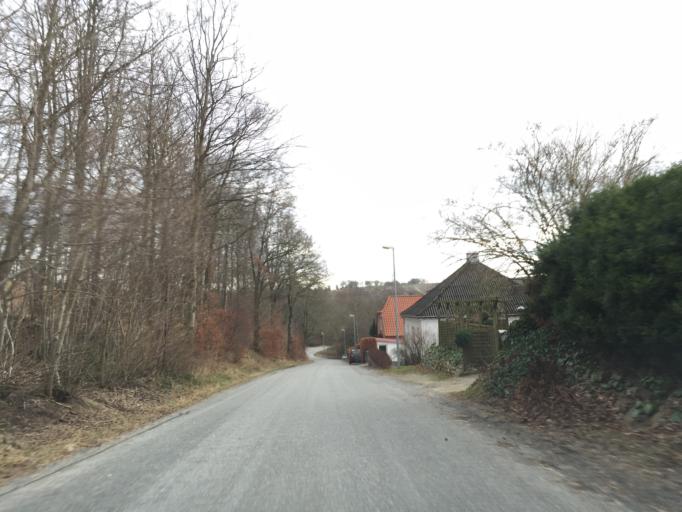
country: DK
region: Central Jutland
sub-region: Viborg Kommune
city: Viborg
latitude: 56.3699
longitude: 9.3210
